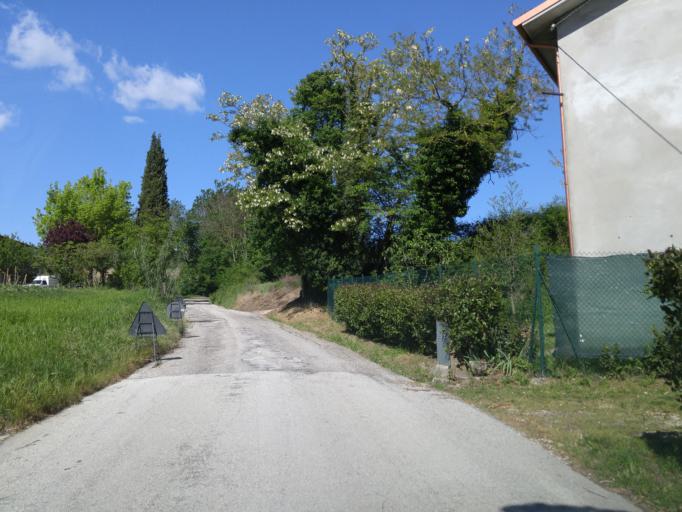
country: IT
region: The Marches
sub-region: Provincia di Pesaro e Urbino
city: Cartoceto
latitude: 43.7826
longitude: 12.9055
